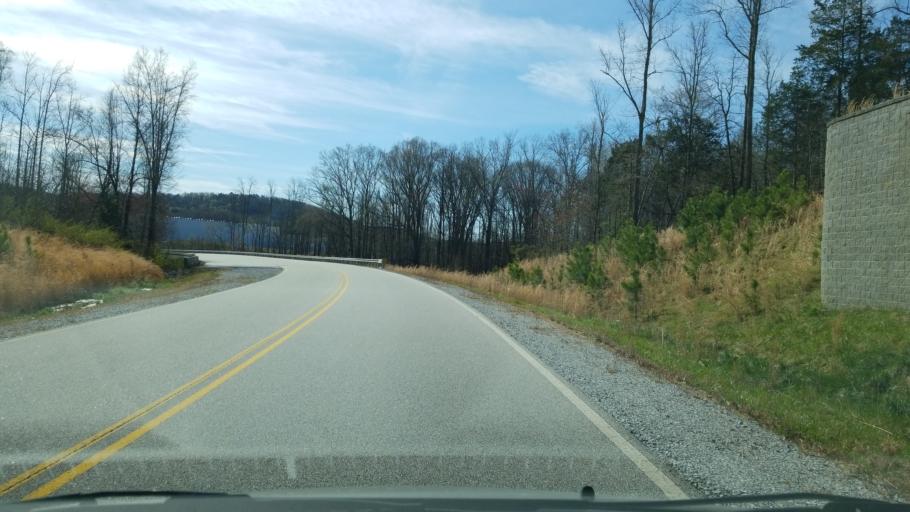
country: US
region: Tennessee
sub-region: Hamilton County
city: Harrison
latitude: 35.0962
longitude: -85.1365
